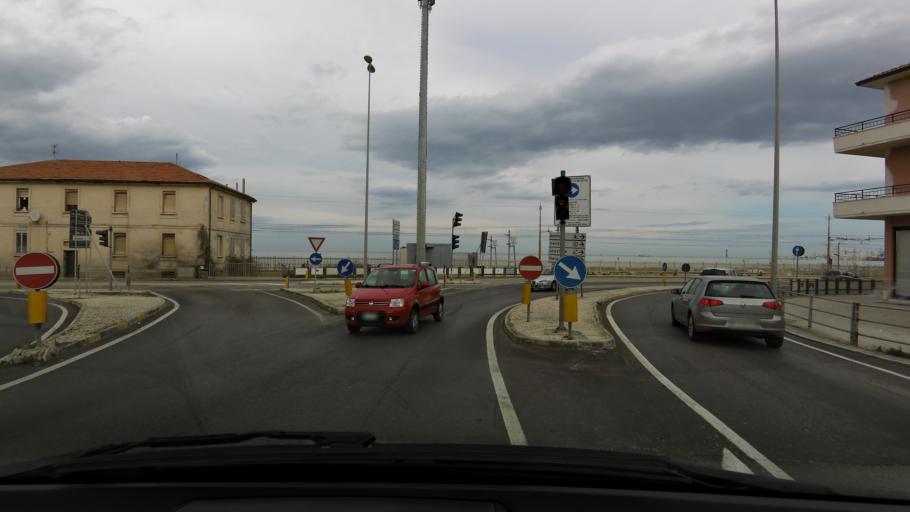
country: IT
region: The Marches
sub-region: Provincia di Ancona
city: Posatora
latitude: 43.6094
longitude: 13.4564
